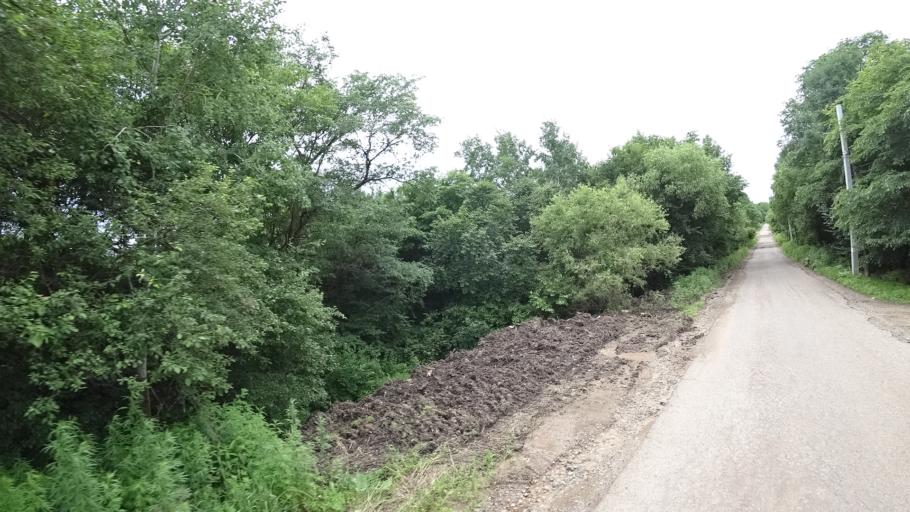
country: RU
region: Primorskiy
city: Novosysoyevka
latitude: 44.2056
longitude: 133.3279
